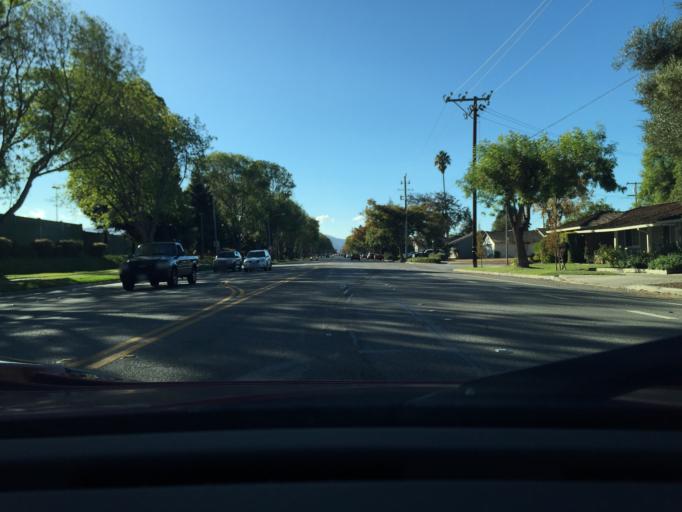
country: US
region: California
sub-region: Santa Clara County
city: Cupertino
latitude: 37.3378
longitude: -122.0062
